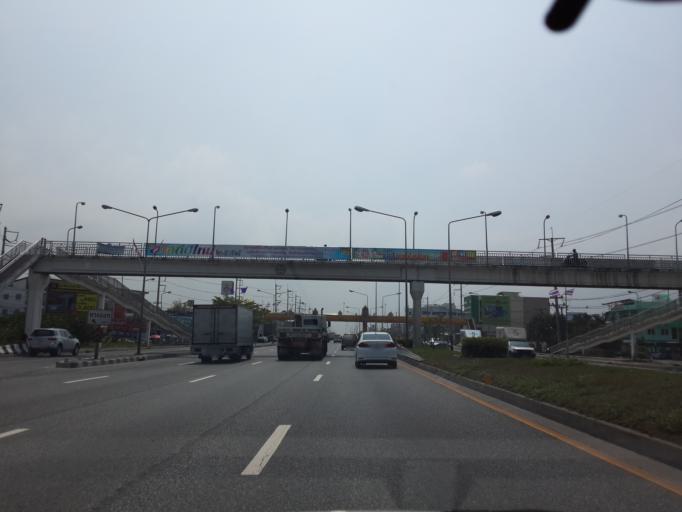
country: TH
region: Chon Buri
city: Chon Buri
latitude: 13.4020
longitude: 101.0043
